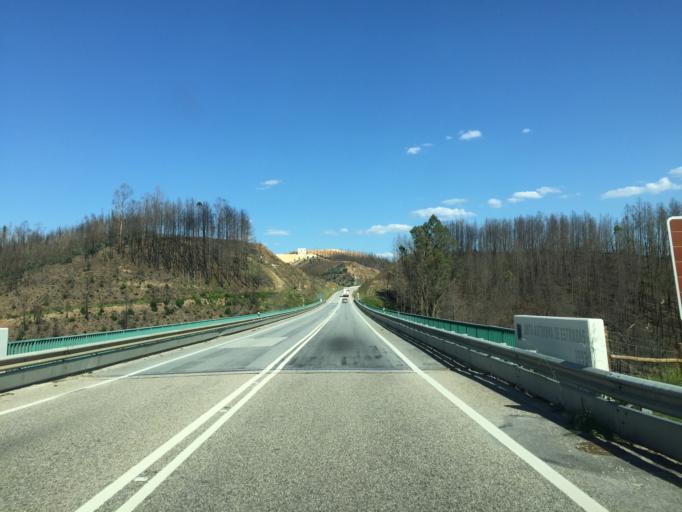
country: PT
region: Leiria
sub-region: Pedrogao Grande
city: Pedrogao Grande
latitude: 39.9267
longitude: -8.1644
